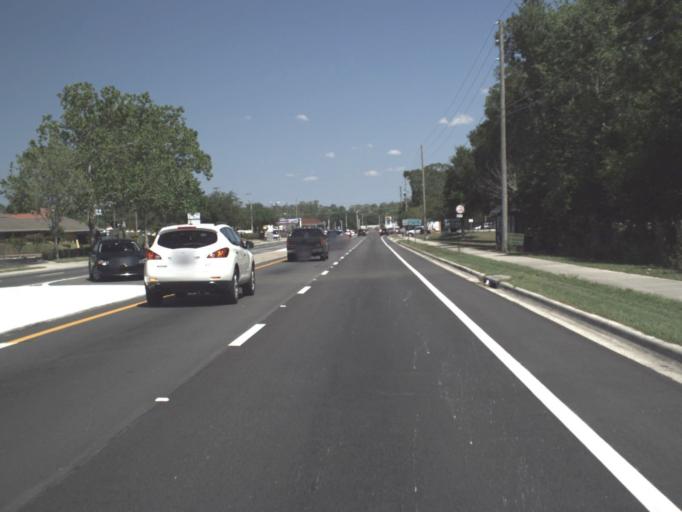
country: US
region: Florida
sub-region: Orange County
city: Azalea Park
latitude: 28.5173
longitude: -81.2937
